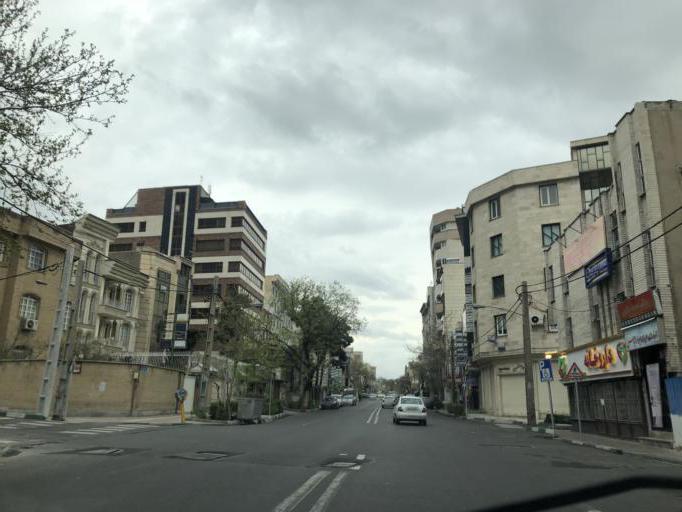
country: IR
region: Tehran
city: Tajrish
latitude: 35.7804
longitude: 51.4612
